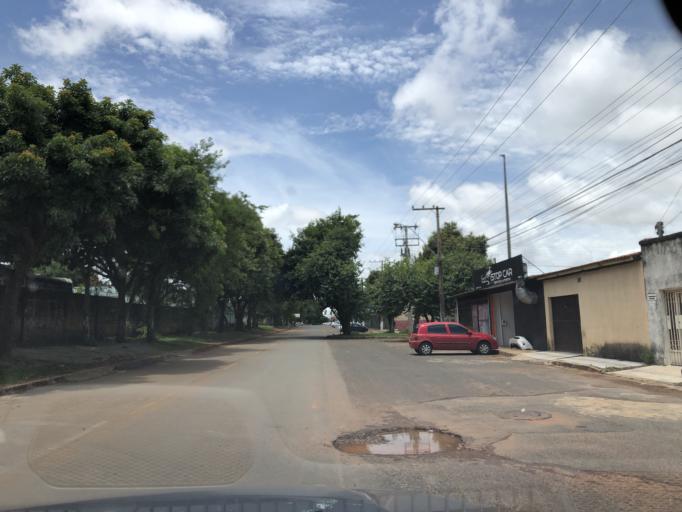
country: BR
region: Federal District
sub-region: Brasilia
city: Brasilia
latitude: -15.8380
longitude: -48.1107
